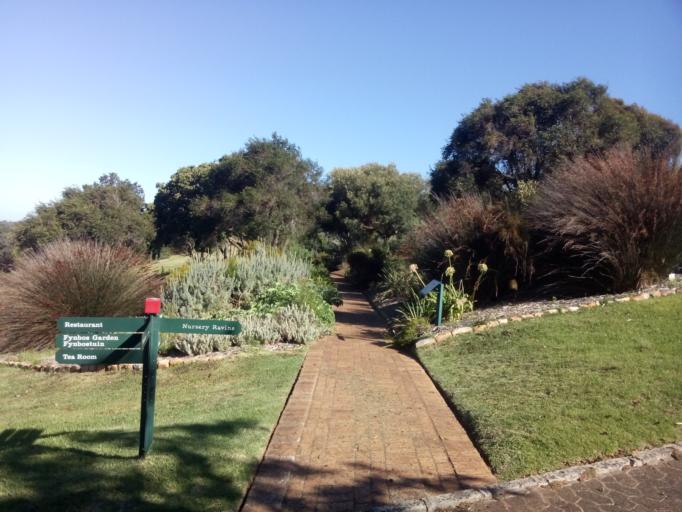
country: ZA
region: Western Cape
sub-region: City of Cape Town
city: Newlands
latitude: -33.9886
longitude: 18.4260
